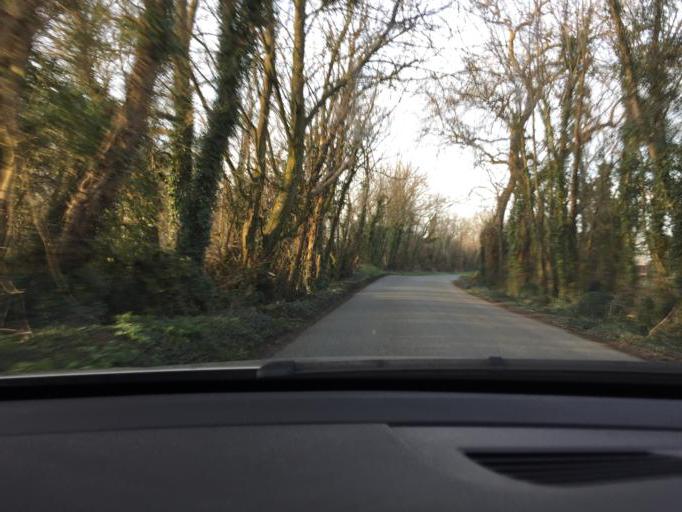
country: IE
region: Leinster
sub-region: An Mhi
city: Dunboyne
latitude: 53.4356
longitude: -6.4524
